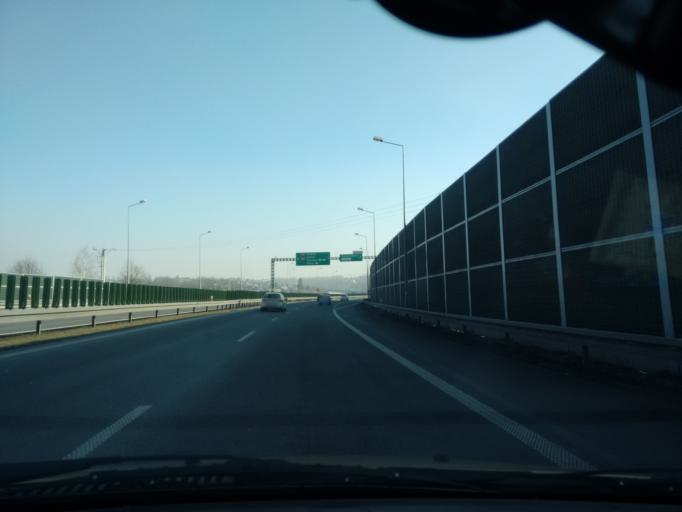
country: PL
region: Silesian Voivodeship
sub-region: Bielsko-Biala
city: Bielsko-Biala
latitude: 49.8468
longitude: 19.0629
